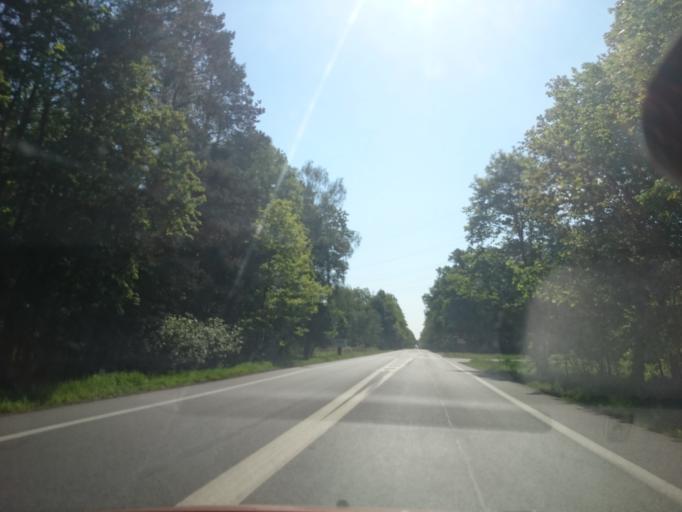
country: PL
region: Opole Voivodeship
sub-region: Powiat opolski
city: Chrzastowice
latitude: 50.6295
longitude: 18.0298
